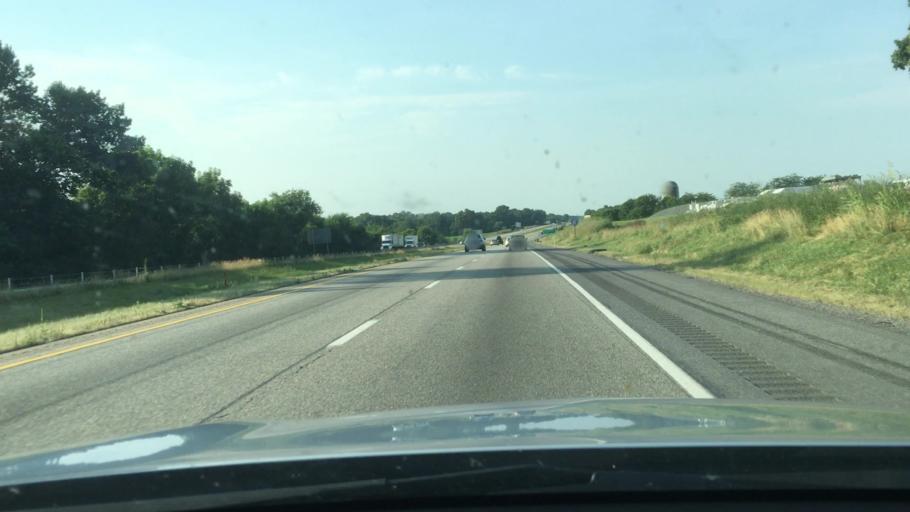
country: US
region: Pennsylvania
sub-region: Franklin County
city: Greencastle
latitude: 39.7945
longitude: -77.7108
